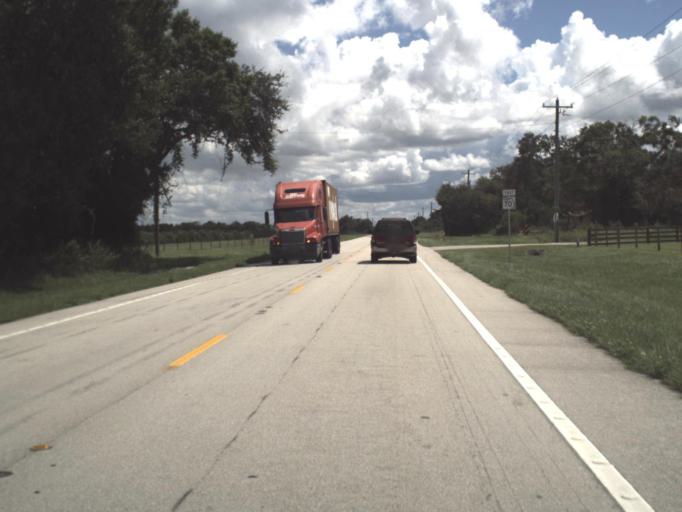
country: US
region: Florida
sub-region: DeSoto County
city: Arcadia
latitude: 27.2639
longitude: -81.9885
